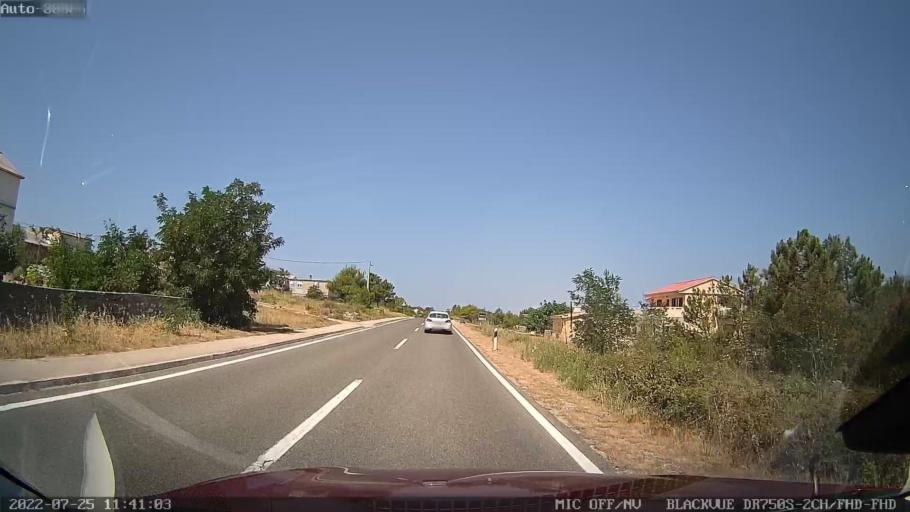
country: HR
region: Zadarska
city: Razanac
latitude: 44.2666
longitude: 15.3518
